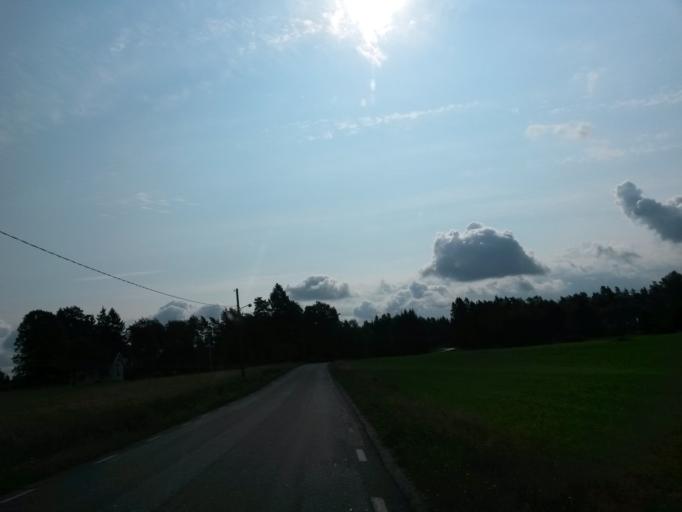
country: SE
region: Vaestra Goetaland
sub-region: Vargarda Kommun
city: Jonstorp
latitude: 58.0134
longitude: 12.6566
